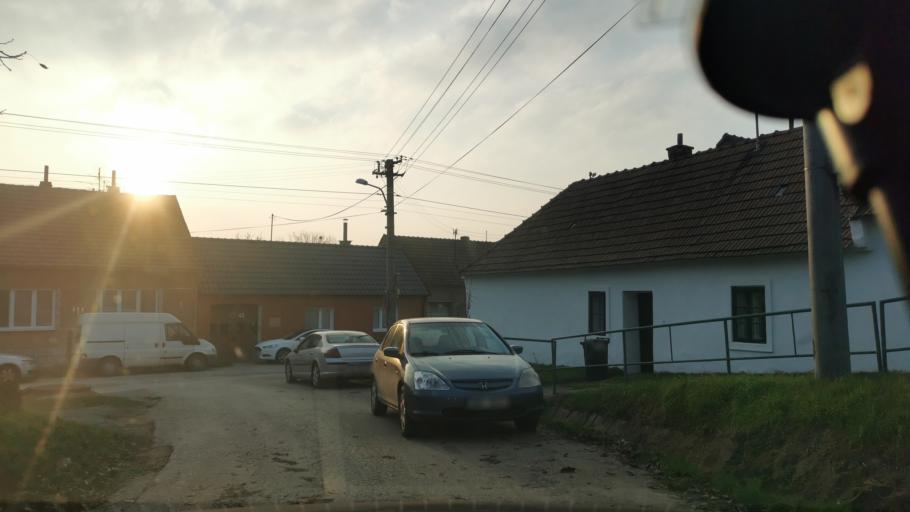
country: SK
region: Trnavsky
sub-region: Okres Skalica
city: Skalica
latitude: 48.7874
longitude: 17.2205
